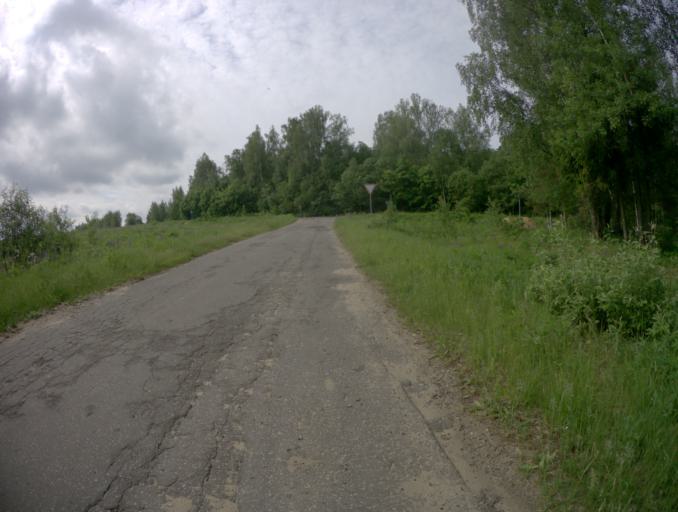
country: RU
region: Vladimir
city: Lakinsk
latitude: 56.0645
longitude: 39.9398
